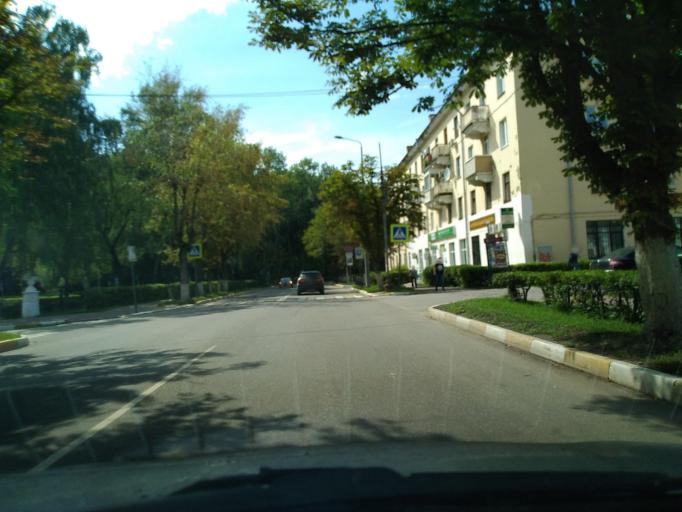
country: RU
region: Moskovskaya
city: Voskresensk
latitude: 55.3234
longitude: 38.6732
